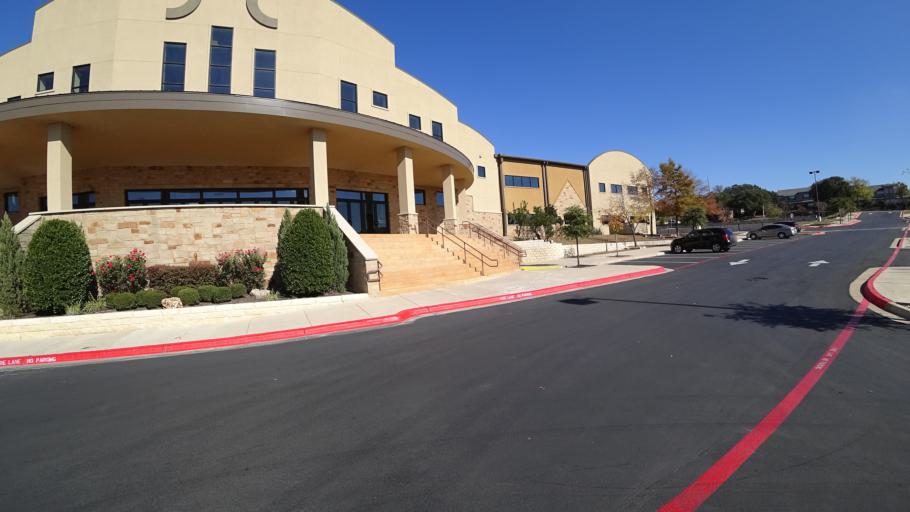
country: US
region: Texas
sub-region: Travis County
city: Wells Branch
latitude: 30.4362
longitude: -97.6980
